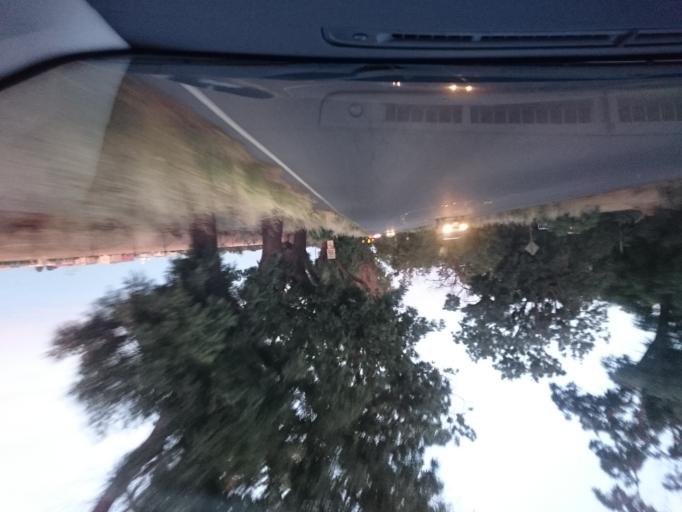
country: US
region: California
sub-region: Yolo County
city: Davis
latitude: 38.5465
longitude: -121.7820
